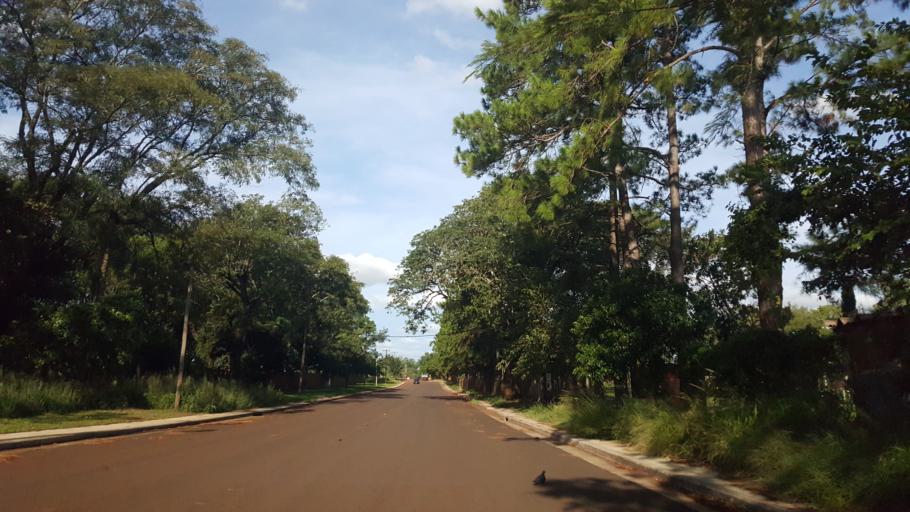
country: AR
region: Misiones
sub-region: Departamento de Capital
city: Posadas
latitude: -27.3614
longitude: -55.9564
